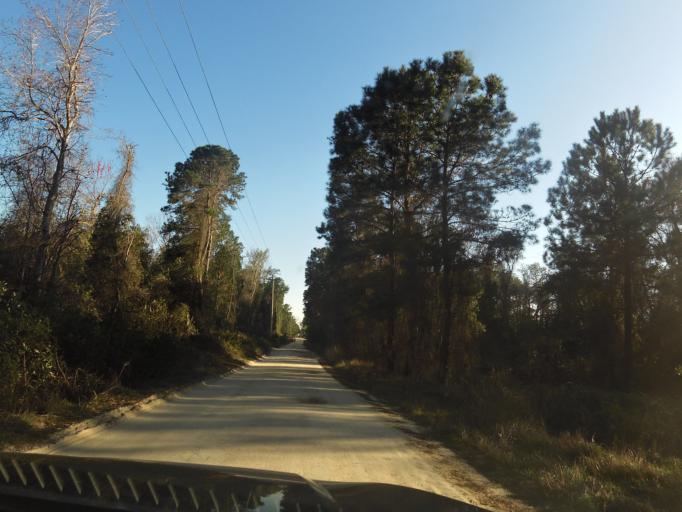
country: US
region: Florida
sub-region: Clay County
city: Middleburg
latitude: 30.1386
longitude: -81.8820
